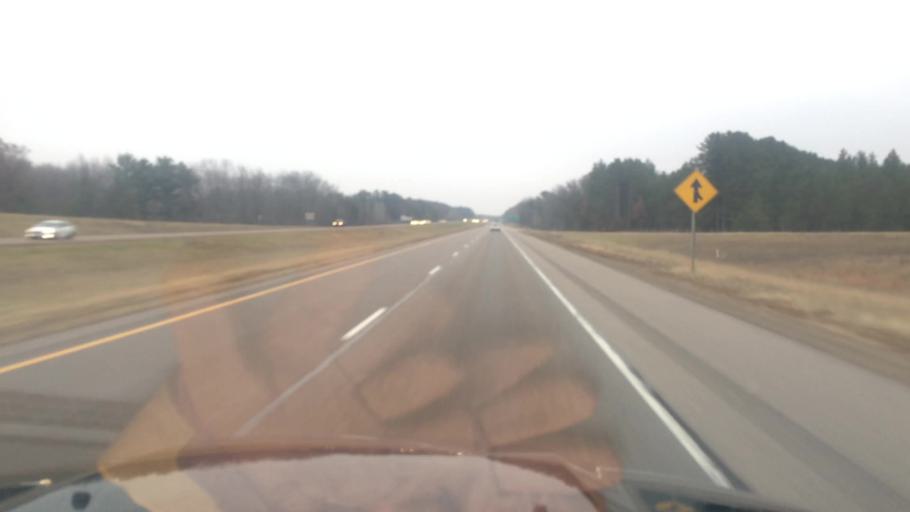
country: US
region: Wisconsin
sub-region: Portage County
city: Stevens Point
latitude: 44.5698
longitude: -89.5983
